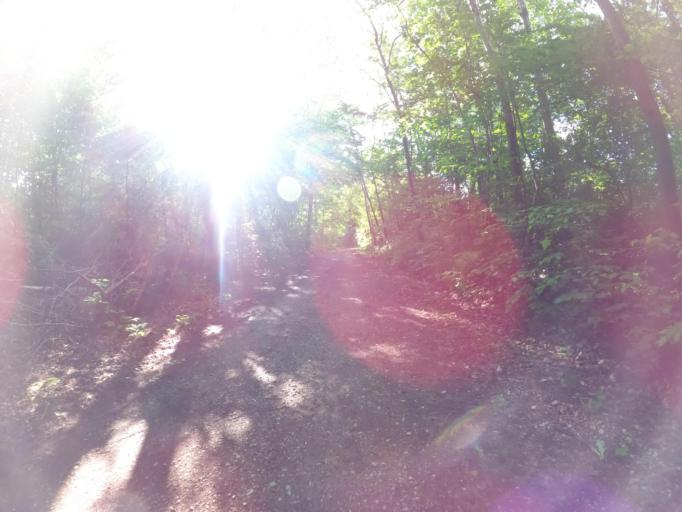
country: PL
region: Warmian-Masurian Voivodeship
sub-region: Powiat lidzbarski
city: Lidzbark Warminski
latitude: 54.1252
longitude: 20.5992
